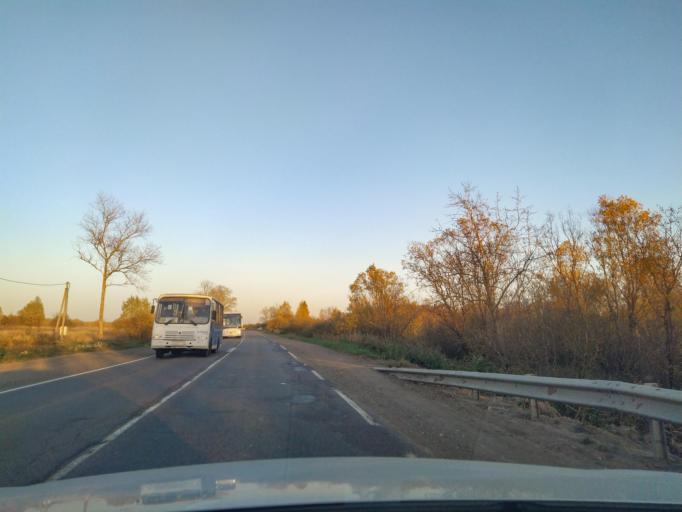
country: RU
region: Leningrad
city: Maloye Verevo
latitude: 59.6116
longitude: 30.2302
